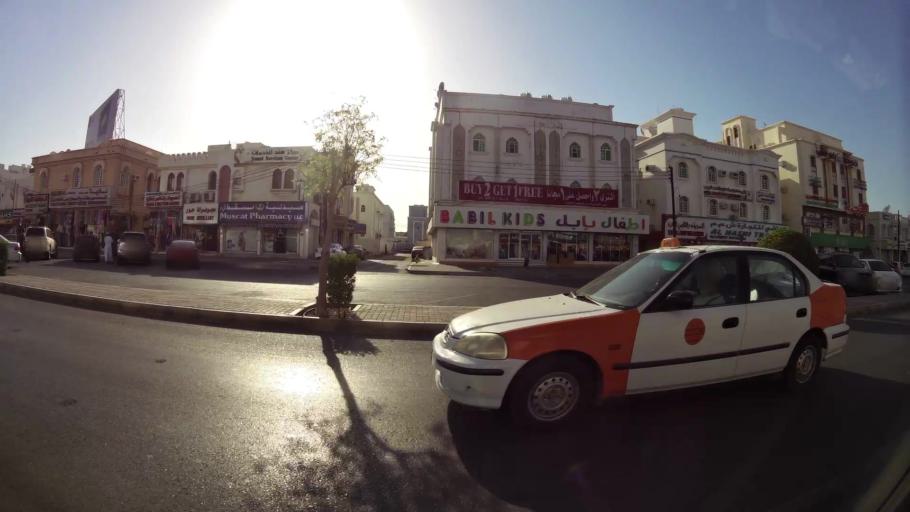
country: OM
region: Muhafazat Masqat
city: As Sib al Jadidah
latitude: 23.6329
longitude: 58.1993
